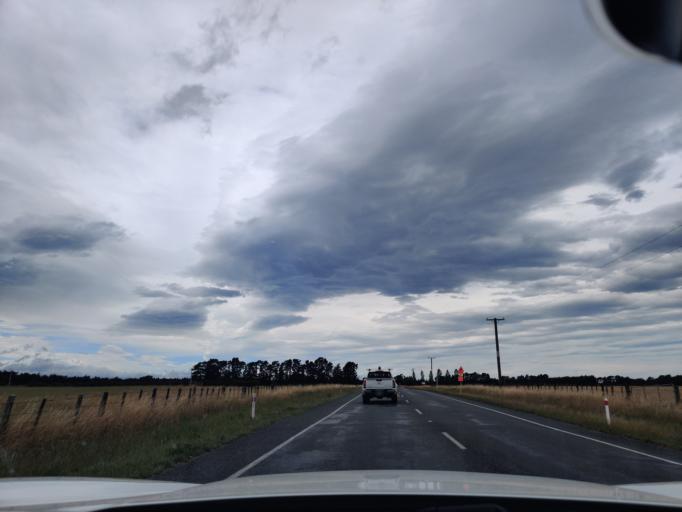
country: NZ
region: Wellington
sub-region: Masterton District
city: Masterton
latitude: -40.9988
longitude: 175.5583
